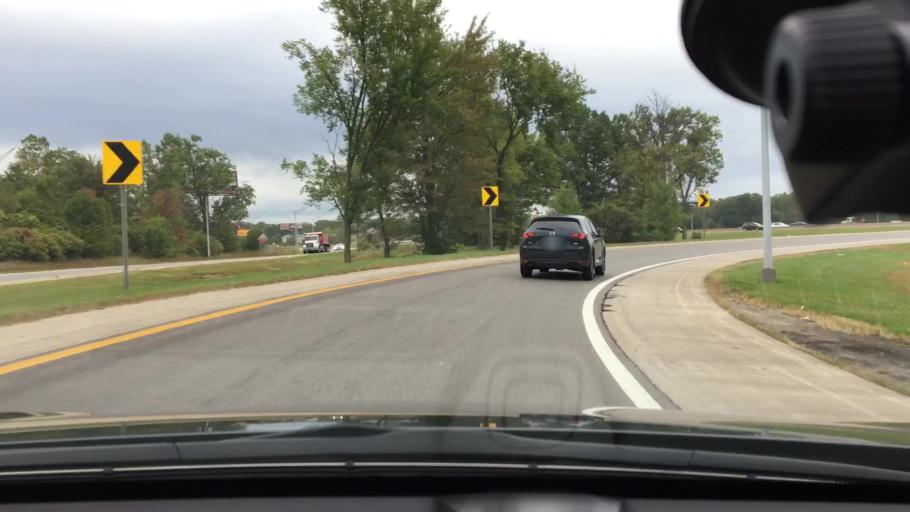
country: US
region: Michigan
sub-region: Wayne County
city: Inkster
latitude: 42.2446
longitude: -83.3265
